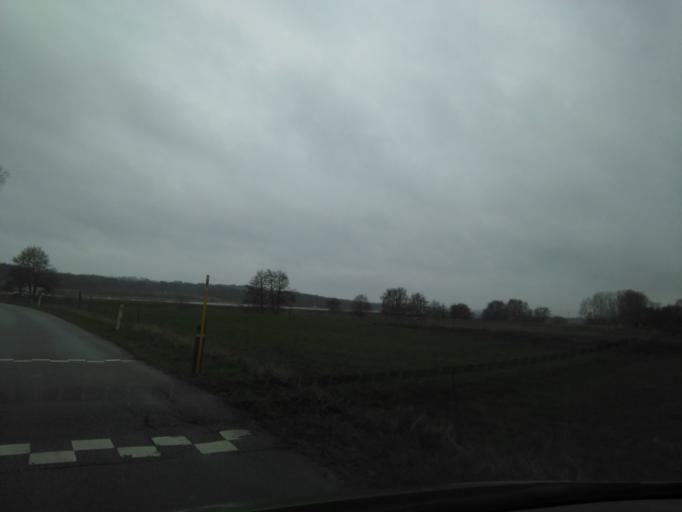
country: DK
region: Central Jutland
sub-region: Arhus Kommune
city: Stavtrup
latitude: 56.1488
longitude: 10.0890
